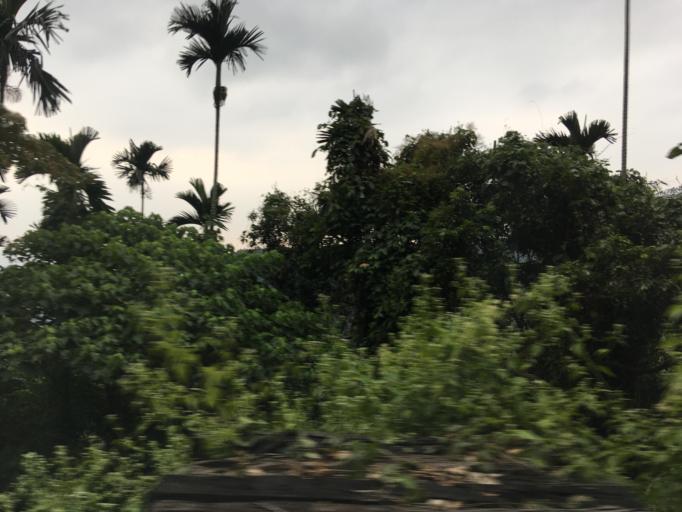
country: TW
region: Taiwan
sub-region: Chiayi
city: Jiayi Shi
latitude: 23.5343
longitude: 120.6062
